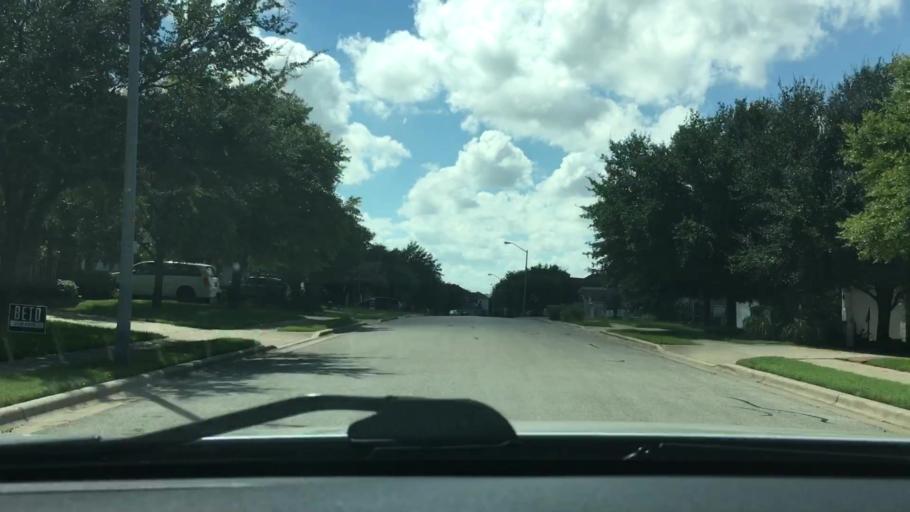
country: US
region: Texas
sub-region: Travis County
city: Windemere
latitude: 30.4752
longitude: -97.6528
